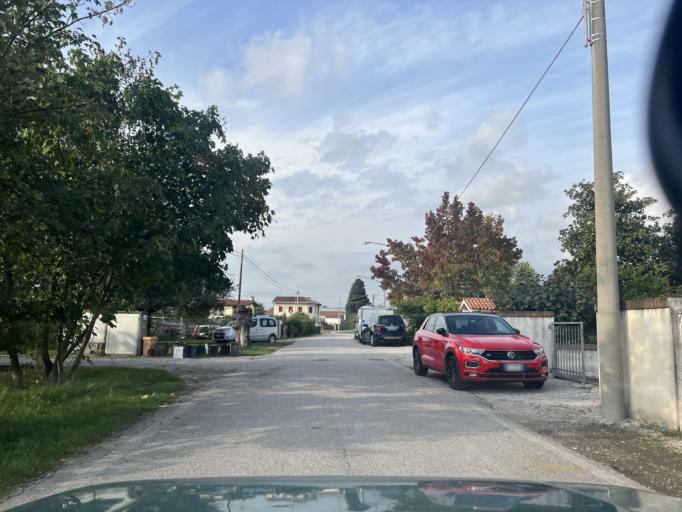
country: IT
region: Friuli Venezia Giulia
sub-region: Provincia di Gorizia
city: Mossa
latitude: 45.9346
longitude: 13.5551
